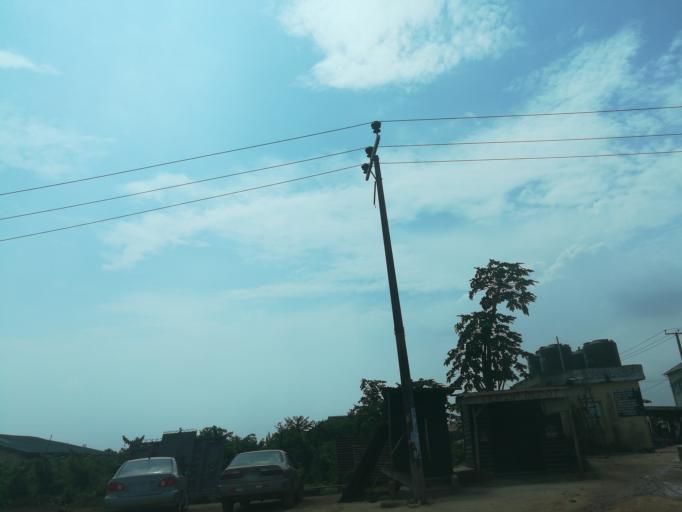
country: NG
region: Lagos
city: Ikorodu
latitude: 6.5959
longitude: 3.6248
